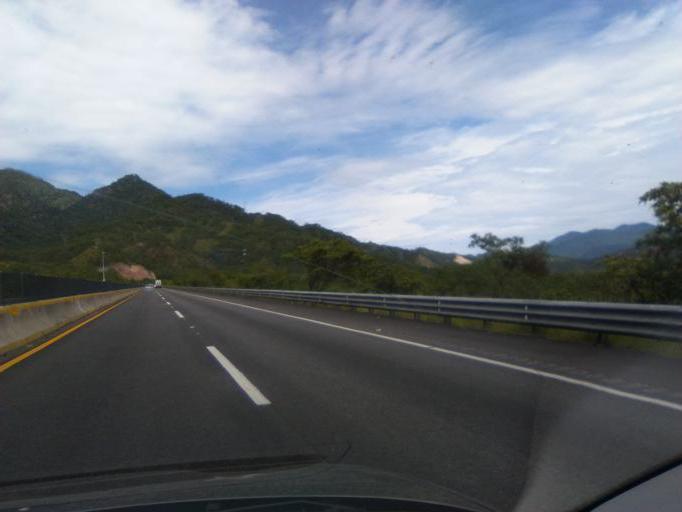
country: MX
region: Guerrero
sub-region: Chilpancingo de los Bravo
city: Cajelitos
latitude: 17.2931
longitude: -99.5043
